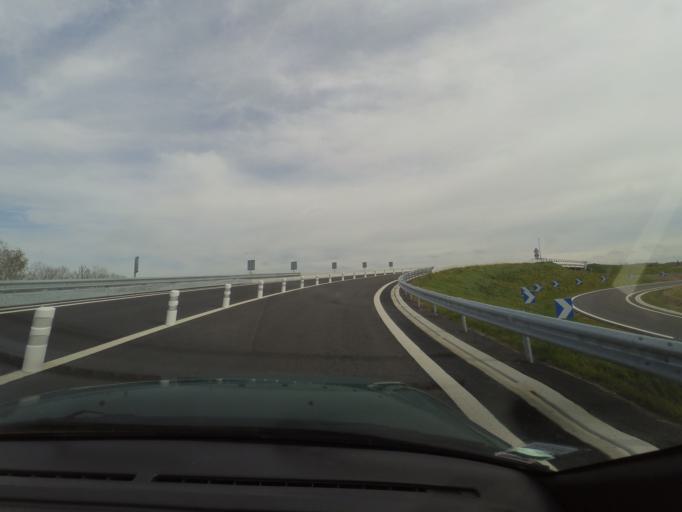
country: FR
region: Pays de la Loire
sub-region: Departement de la Loire-Atlantique
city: Aigrefeuille-sur-Maine
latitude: 47.0717
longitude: -1.4387
